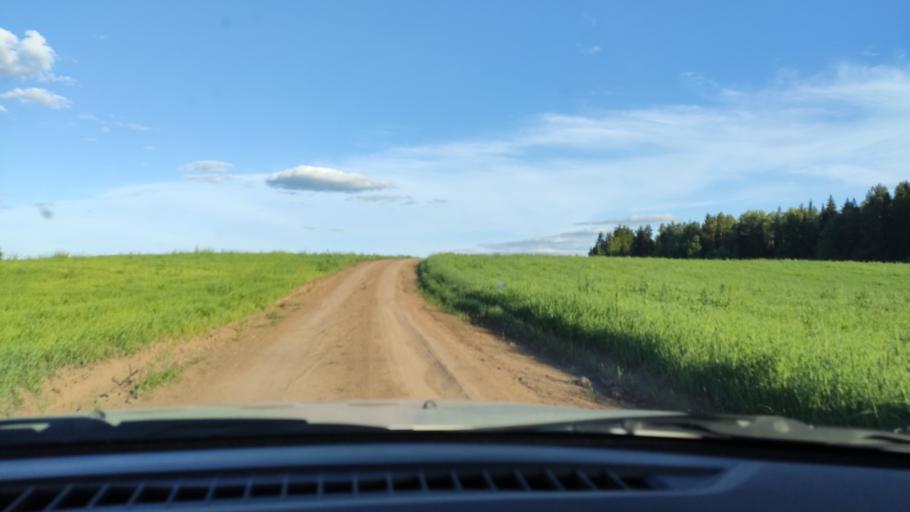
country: RU
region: Perm
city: Orda
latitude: 57.2985
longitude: 56.5922
